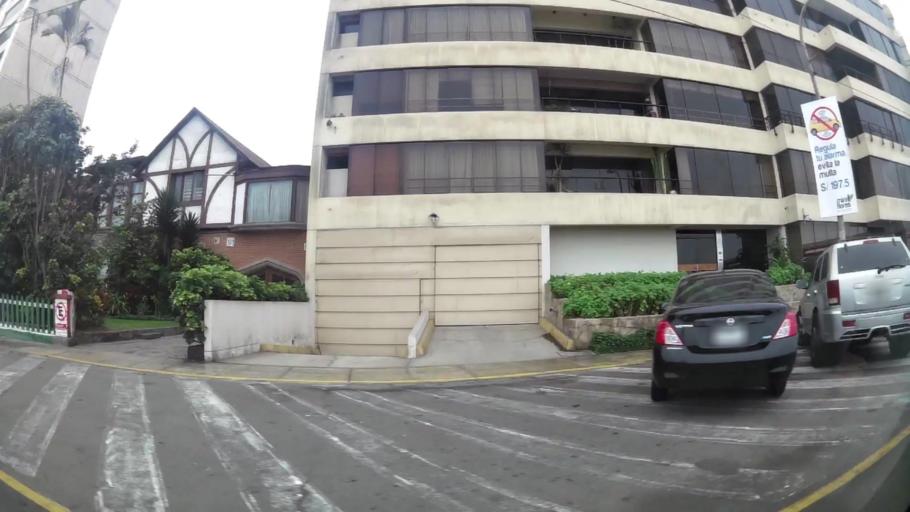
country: PE
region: Lima
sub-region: Lima
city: San Isidro
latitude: -12.1295
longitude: -77.0344
